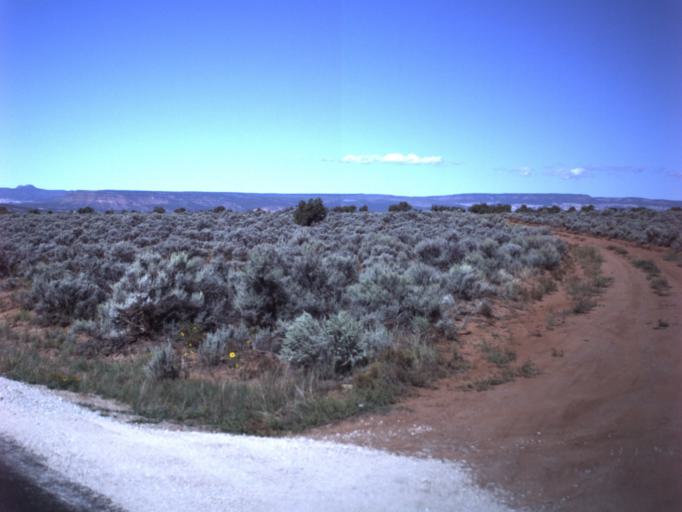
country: US
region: Utah
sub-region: San Juan County
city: Blanding
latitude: 37.5751
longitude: -109.5409
